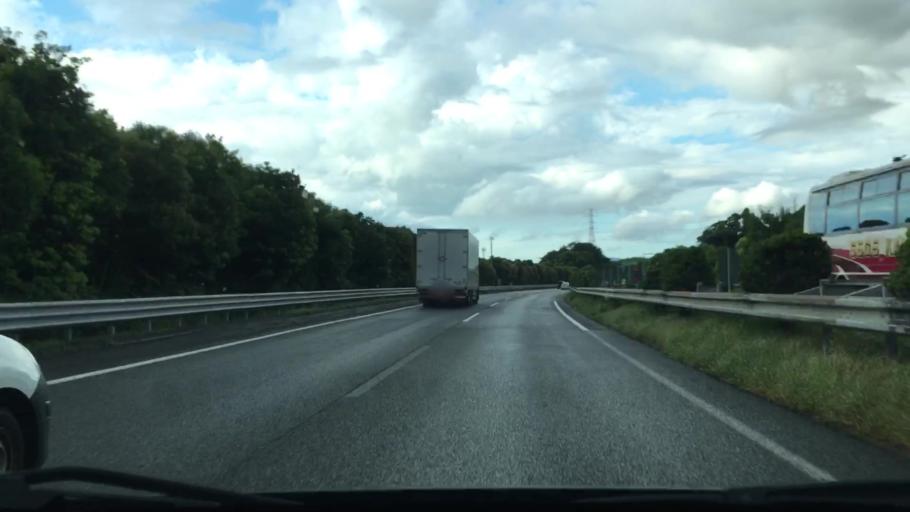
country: JP
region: Fukuoka
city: Koga
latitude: 33.7016
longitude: 130.4851
